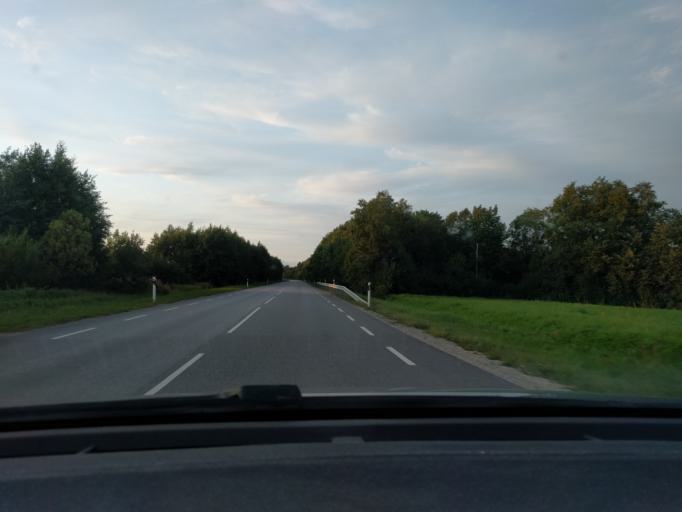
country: EE
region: Paernumaa
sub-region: Sauga vald
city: Sauga
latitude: 58.4137
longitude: 24.4414
